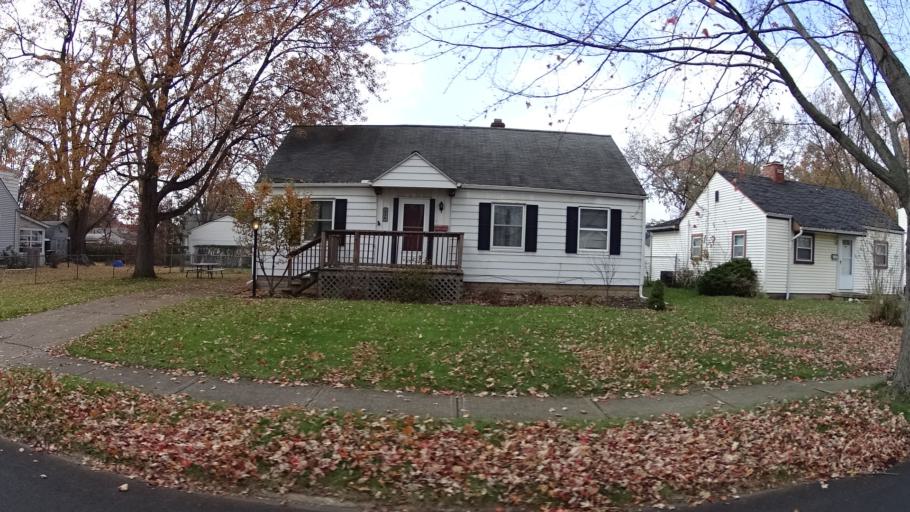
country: US
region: Ohio
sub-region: Lorain County
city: Elyria
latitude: 41.3798
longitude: -82.0804
